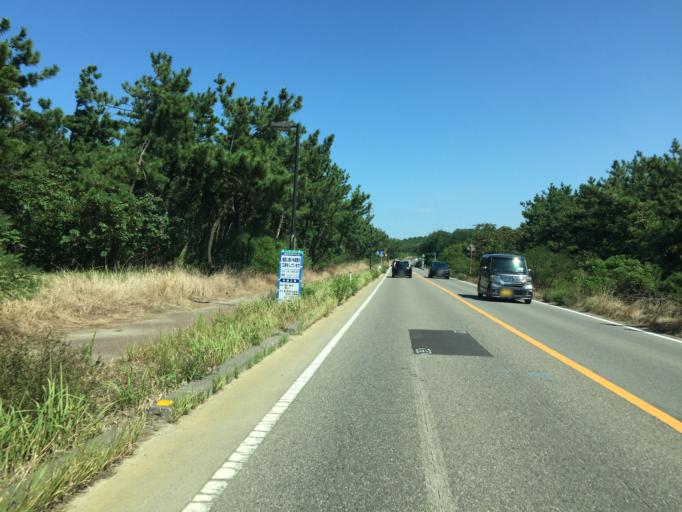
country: JP
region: Niigata
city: Niigata-shi
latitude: 37.9044
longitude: 138.9958
